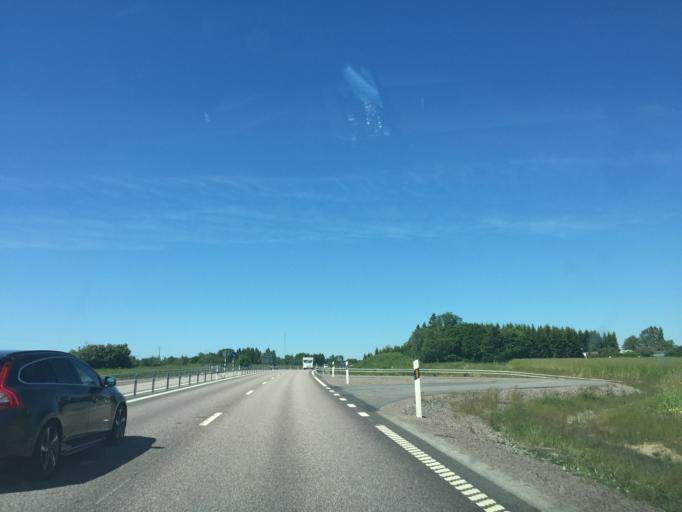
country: SE
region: OEstergoetland
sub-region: Motala Kommun
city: Stenstorp
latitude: 58.4075
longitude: 15.0830
